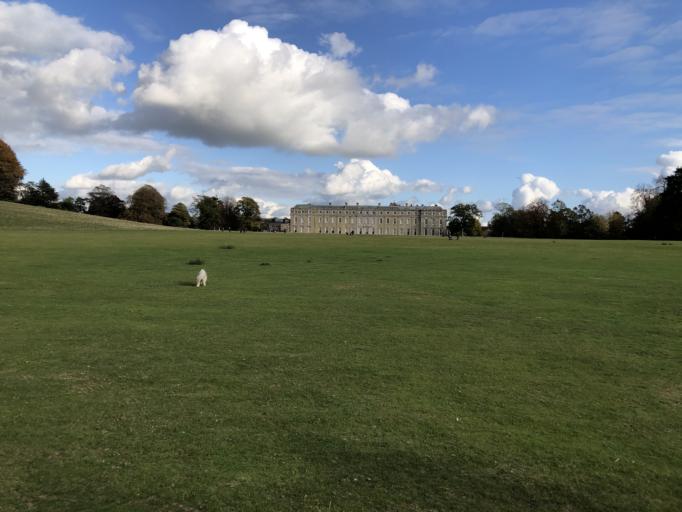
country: GB
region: England
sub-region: West Sussex
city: Petworth
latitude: 50.9887
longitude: -0.6162
